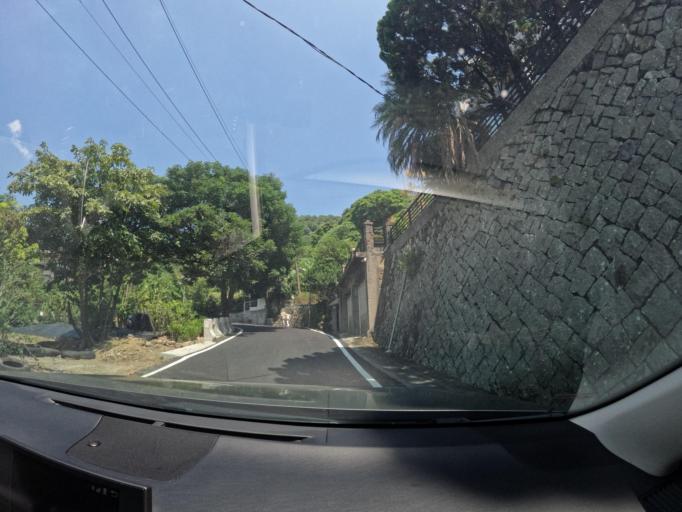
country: TW
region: Taipei
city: Taipei
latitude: 25.1196
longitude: 121.5428
